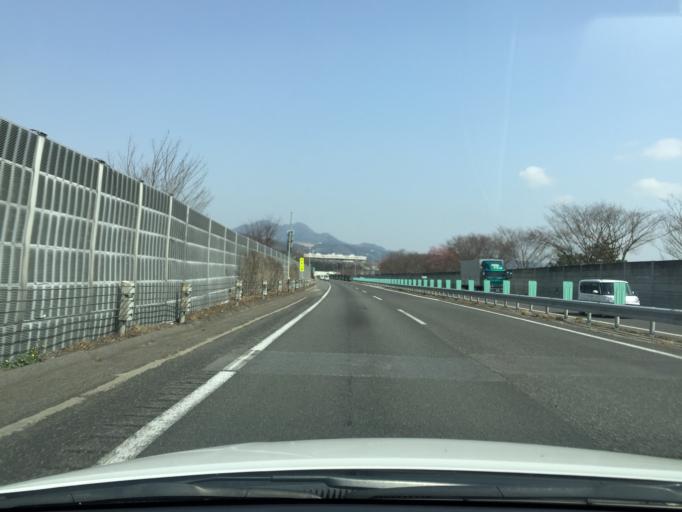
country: JP
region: Miyagi
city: Shiroishi
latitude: 37.9986
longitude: 140.6086
